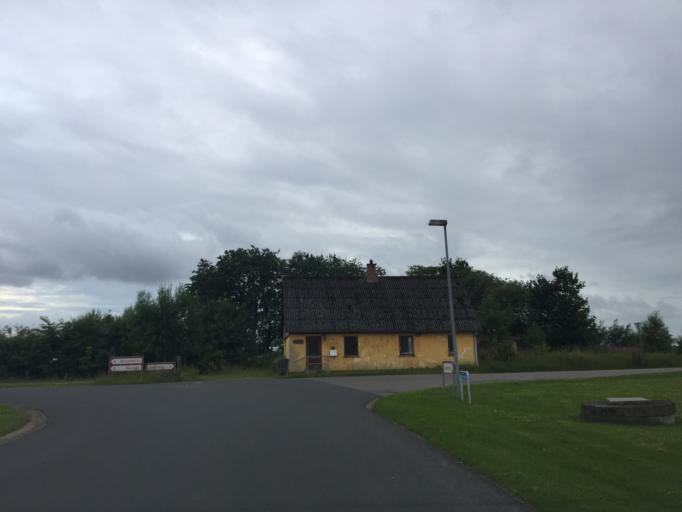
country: DK
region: Central Jutland
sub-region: Silkeborg Kommune
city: Silkeborg
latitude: 56.2356
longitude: 9.5468
